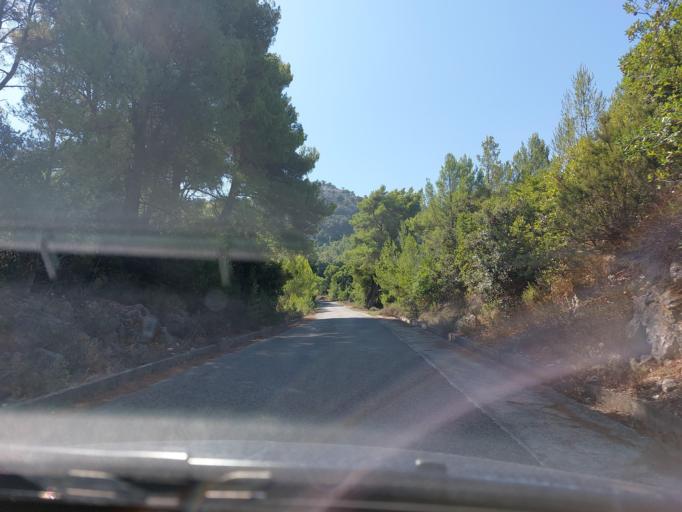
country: HR
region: Dubrovacko-Neretvanska
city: Smokvica
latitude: 42.7465
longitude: 16.8461
